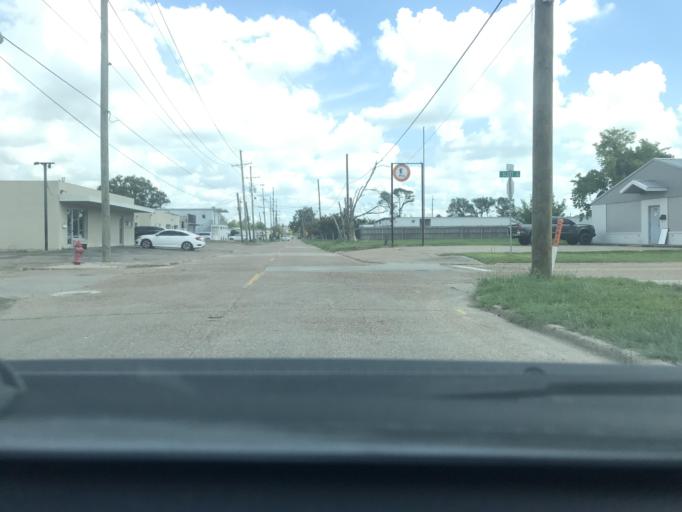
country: US
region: Louisiana
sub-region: Calcasieu Parish
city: Lake Charles
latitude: 30.2111
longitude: -93.2160
